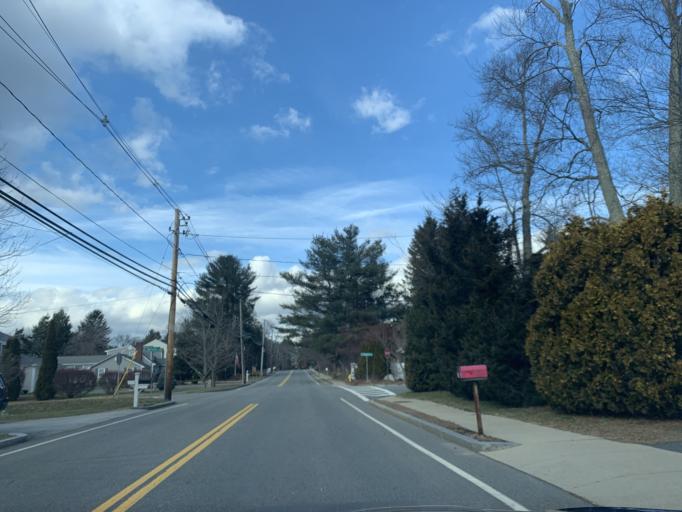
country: US
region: Massachusetts
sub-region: Norfolk County
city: Westwood
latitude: 42.2021
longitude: -71.2196
